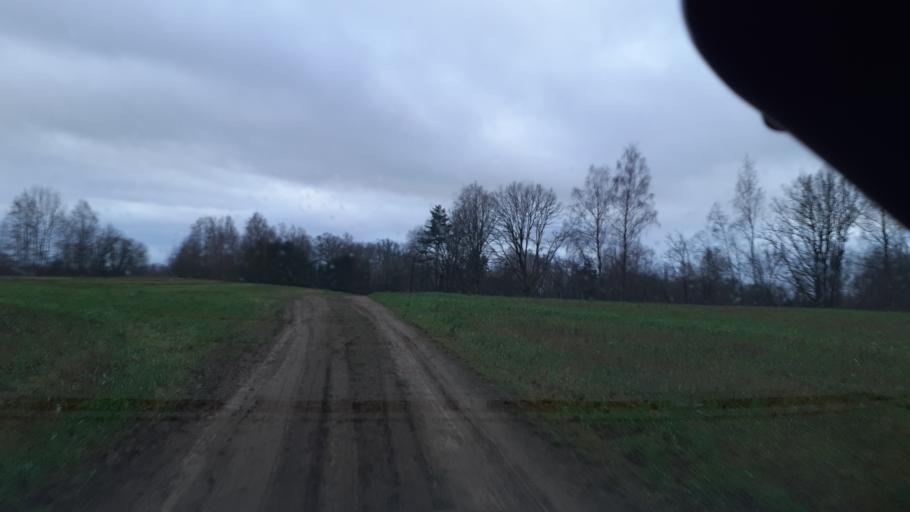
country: LV
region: Kuldigas Rajons
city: Kuldiga
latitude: 56.8813
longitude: 21.7705
